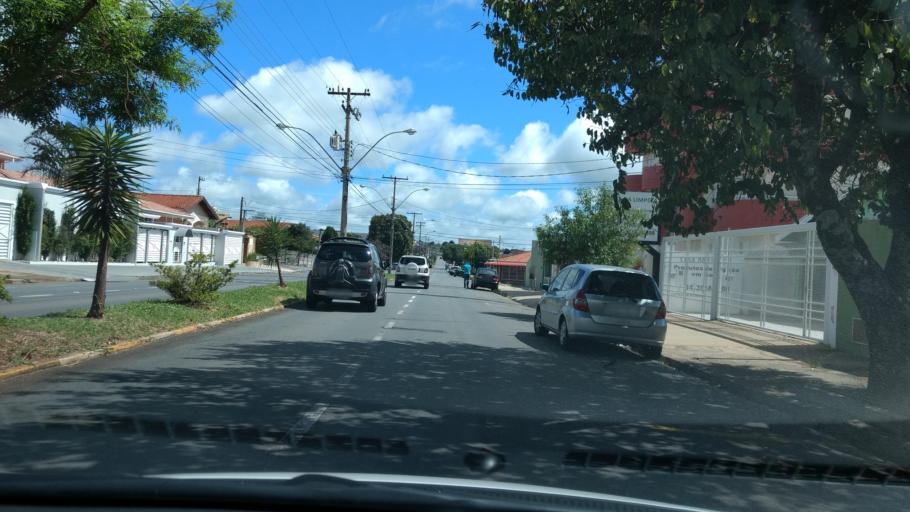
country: BR
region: Sao Paulo
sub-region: Botucatu
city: Botucatu
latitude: -22.8654
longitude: -48.4427
